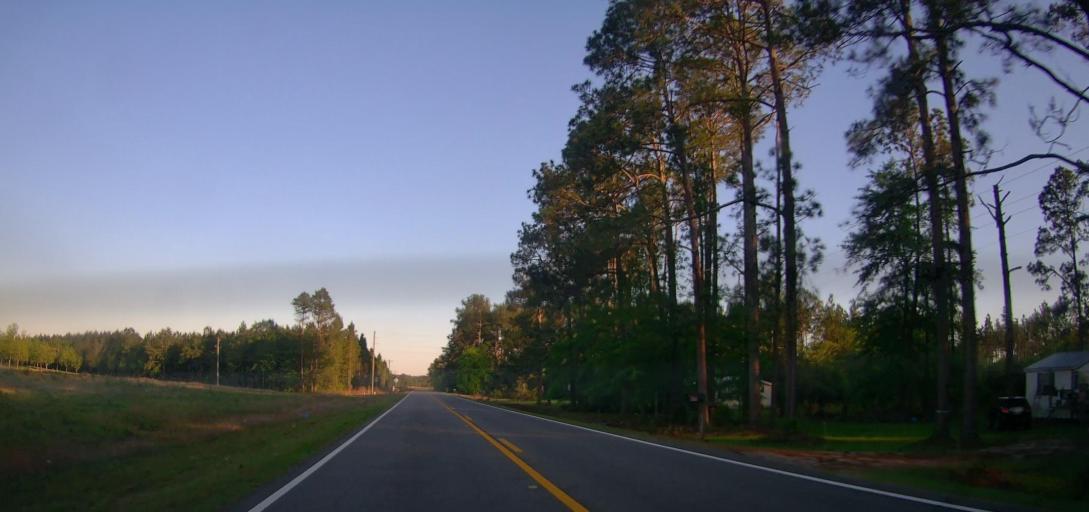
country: US
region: Georgia
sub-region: Irwin County
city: Ocilla
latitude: 31.6203
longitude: -83.2697
